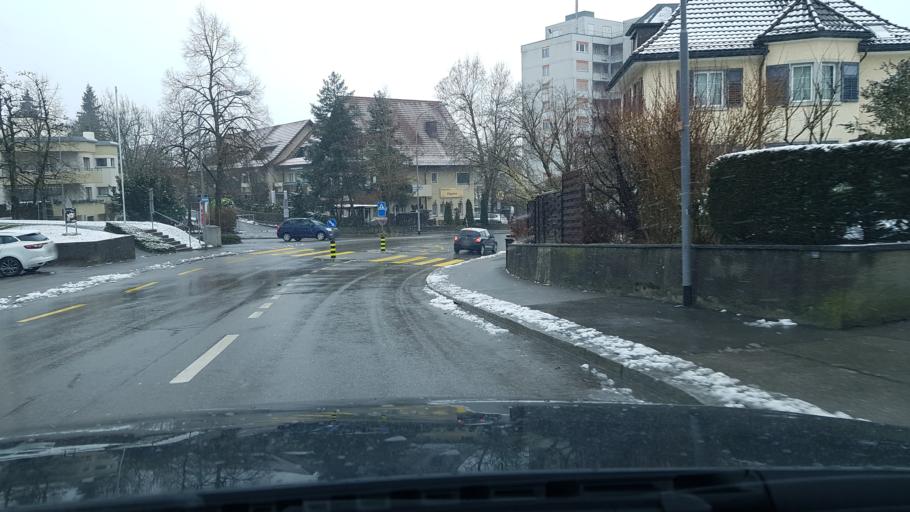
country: CH
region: Zurich
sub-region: Bezirk Zuerich
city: Zuerich (Kreis 11) / Affoltern
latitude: 47.4179
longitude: 8.5064
